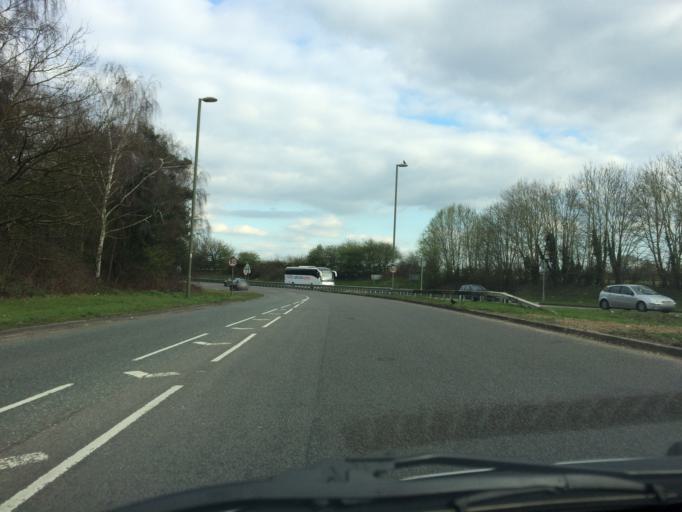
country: GB
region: England
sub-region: Surrey
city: Ottershaw
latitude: 51.3724
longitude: -0.5252
